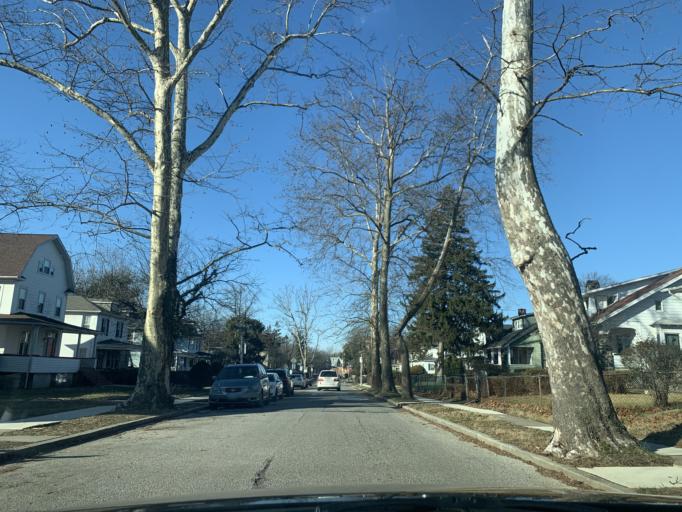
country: US
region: Maryland
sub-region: Baltimore County
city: Lochearn
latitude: 39.3295
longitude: -76.6859
